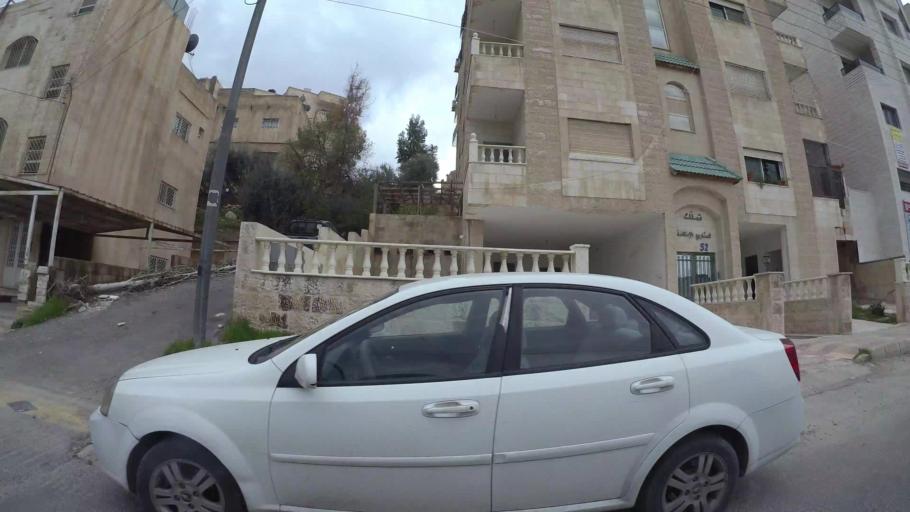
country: JO
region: Amman
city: Amman
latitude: 32.0051
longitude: 35.9498
